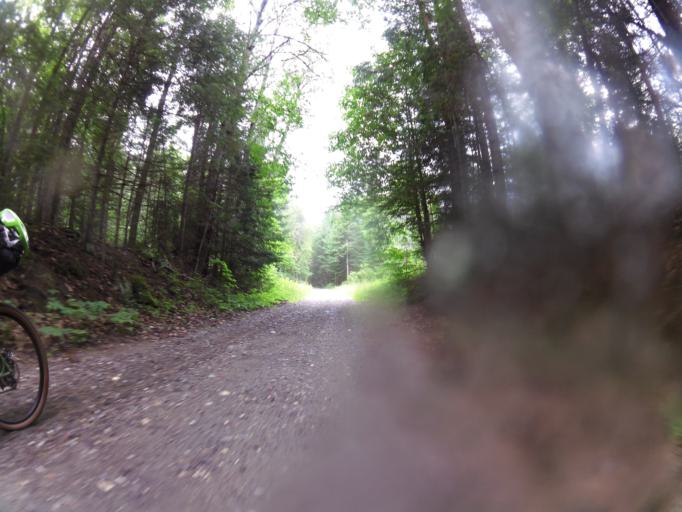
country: CA
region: Ontario
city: Renfrew
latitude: 45.0824
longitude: -76.7211
